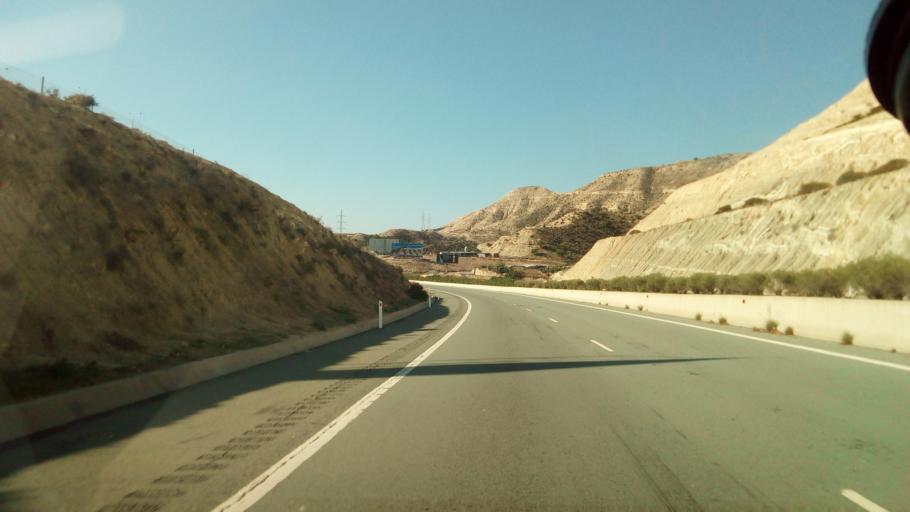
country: CY
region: Limassol
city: Pissouri
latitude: 34.6726
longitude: 32.6618
